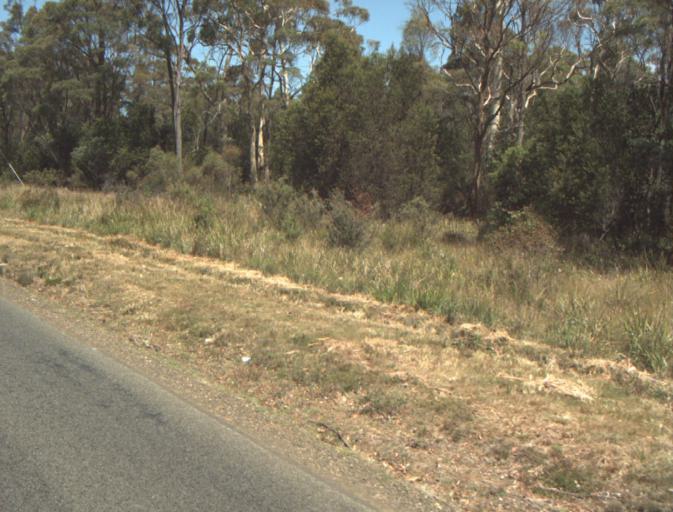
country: AU
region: Tasmania
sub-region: Launceston
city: Mayfield
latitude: -41.3352
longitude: 147.1421
